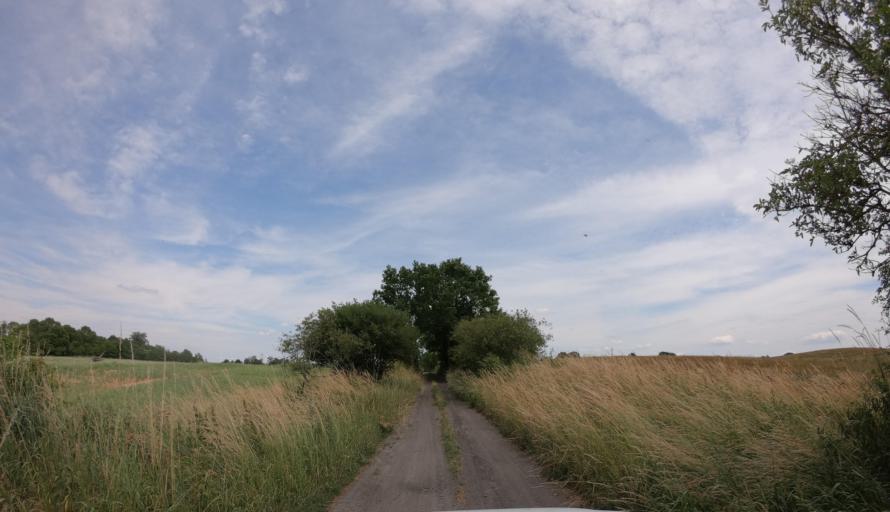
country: PL
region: West Pomeranian Voivodeship
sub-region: Powiat pyrzycki
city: Kozielice
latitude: 53.0303
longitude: 14.7551
